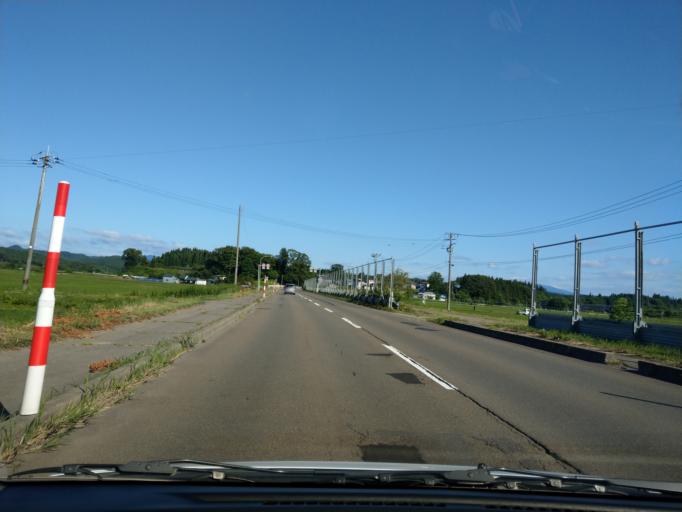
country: JP
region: Akita
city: Takanosu
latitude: 40.1944
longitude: 140.3978
